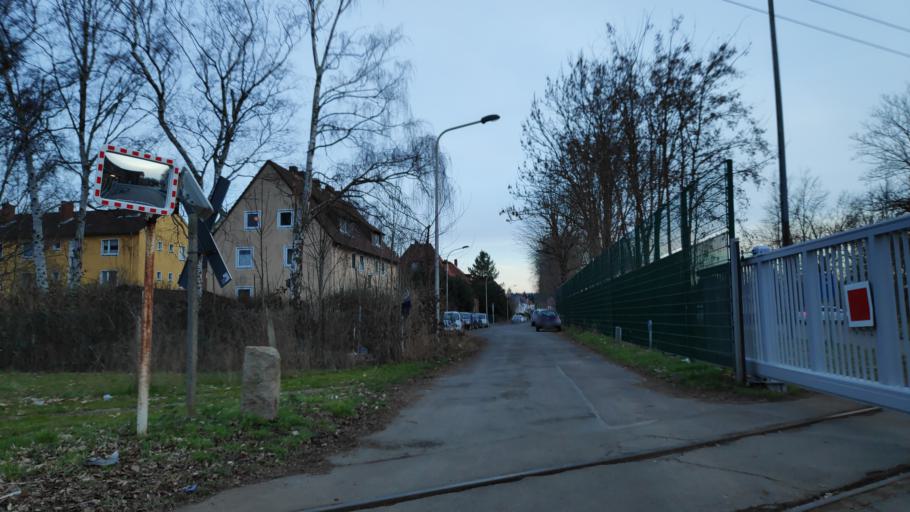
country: DE
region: North Rhine-Westphalia
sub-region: Regierungsbezirk Detmold
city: Minden
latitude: 52.2948
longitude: 8.9417
